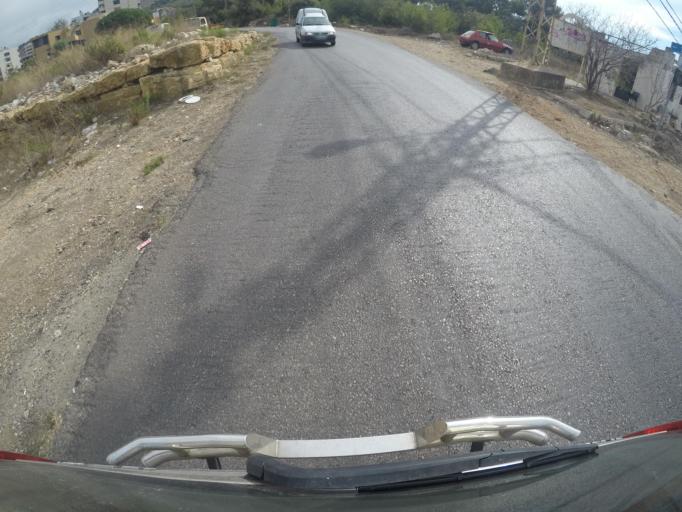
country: LB
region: Mont-Liban
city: Beit ed Dine
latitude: 33.7347
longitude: 35.4876
